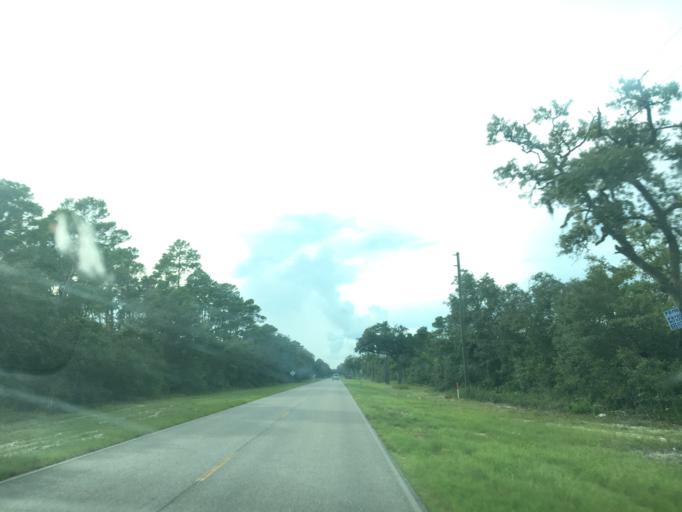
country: US
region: Florida
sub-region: Wakulla County
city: Crawfordville
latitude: 29.9054
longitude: -84.3543
